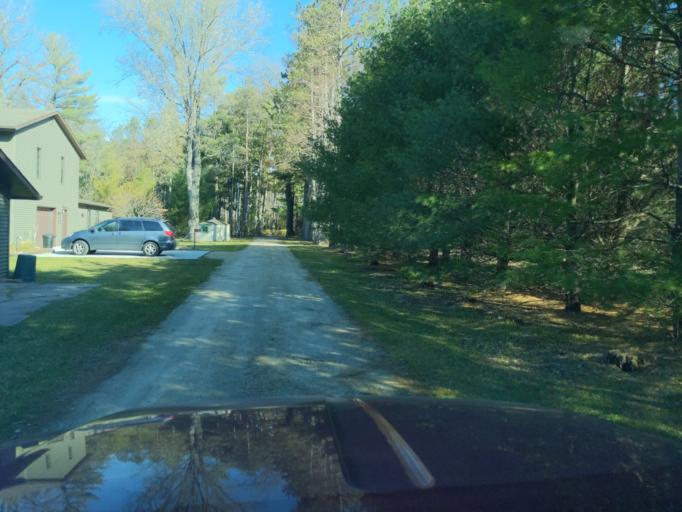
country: US
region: Wisconsin
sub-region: Waushara County
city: Wautoma
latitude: 44.0325
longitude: -89.3011
